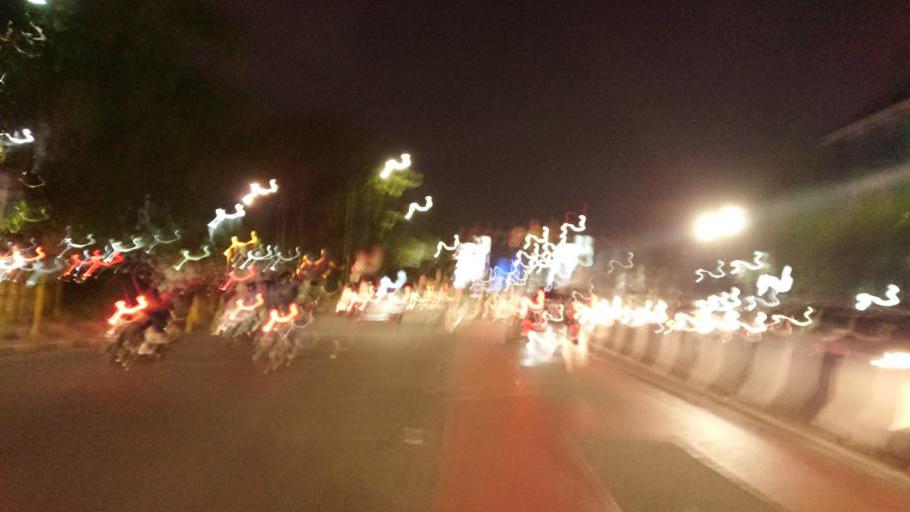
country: ID
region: Jakarta Raya
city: Jakarta
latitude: -6.2442
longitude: 106.7824
